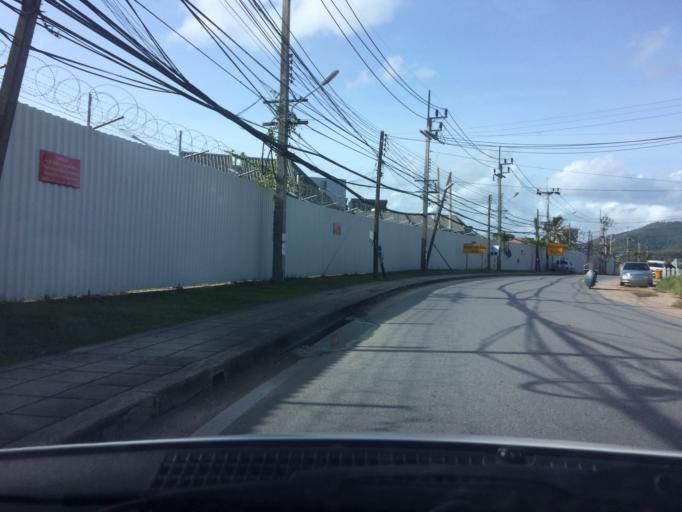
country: TH
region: Phuket
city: Thalang
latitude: 8.1088
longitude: 98.3083
